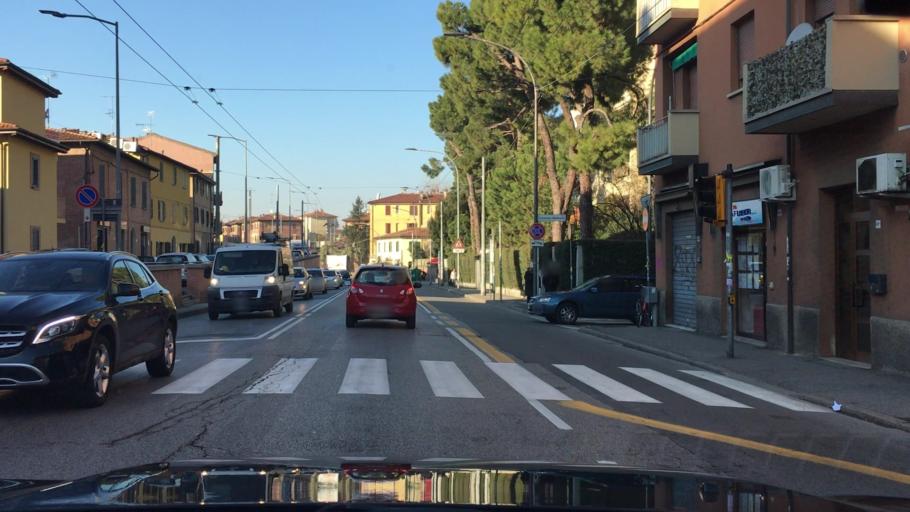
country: IT
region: Emilia-Romagna
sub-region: Provincia di Bologna
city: Ponticella
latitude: 44.4935
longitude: 11.3826
